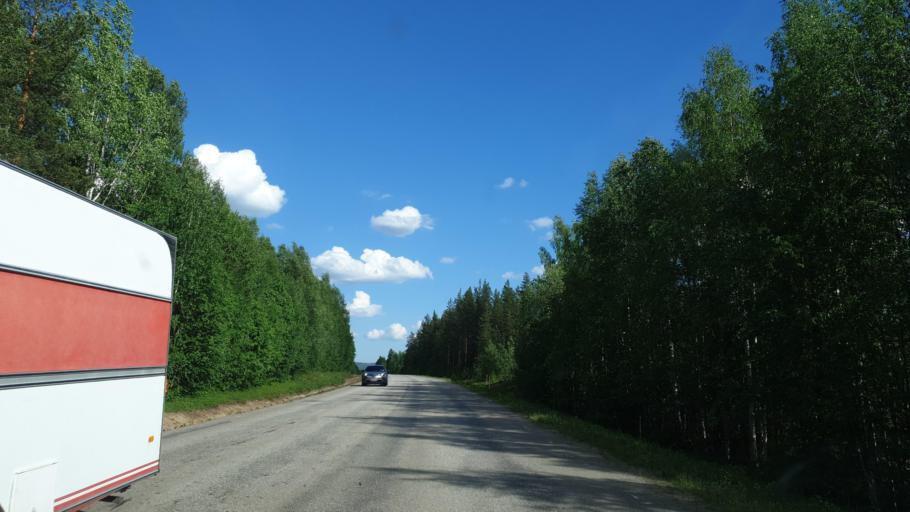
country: SE
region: Norrbotten
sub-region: Alvsbyns Kommun
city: AElvsbyn
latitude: 65.8477
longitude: 20.4635
